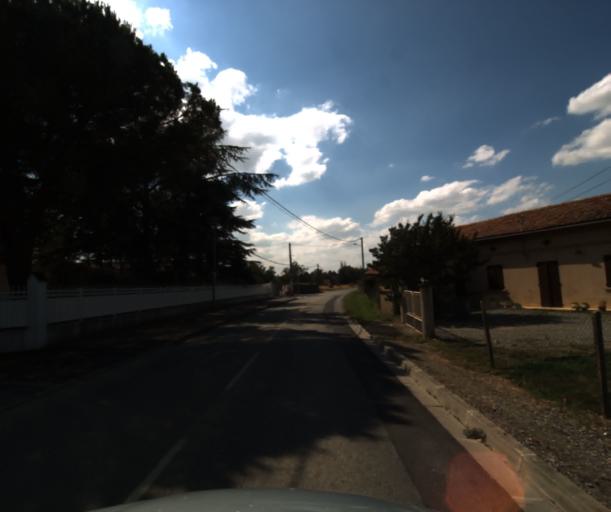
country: FR
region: Midi-Pyrenees
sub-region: Departement de la Haute-Garonne
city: Saint-Lys
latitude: 43.5168
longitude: 1.1707
